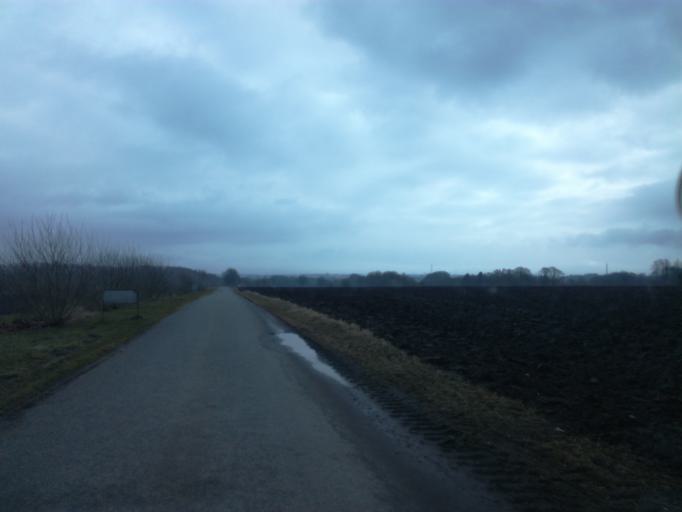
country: DK
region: South Denmark
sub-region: Vejle Kommune
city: Brejning
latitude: 55.6190
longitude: 9.6947
